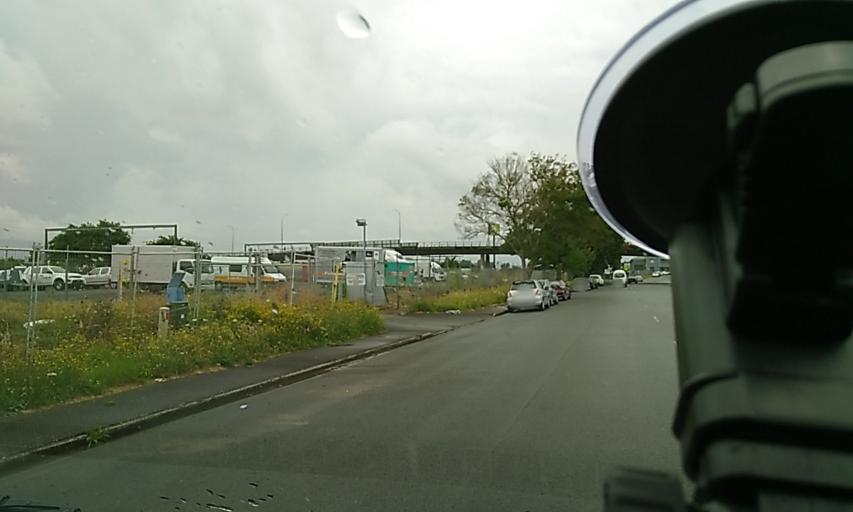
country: NZ
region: Waikato
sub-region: Hamilton City
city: Hamilton
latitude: -37.7887
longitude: 175.2635
